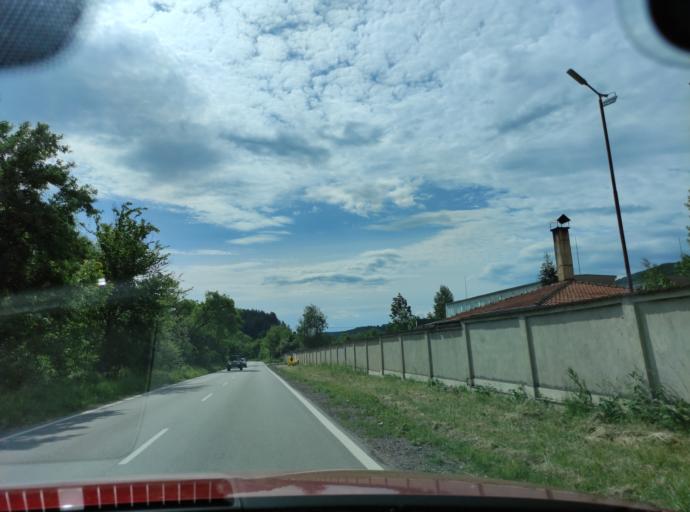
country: BG
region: Montana
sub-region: Obshtina Chiprovtsi
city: Chiprovtsi
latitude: 43.4438
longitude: 22.9269
